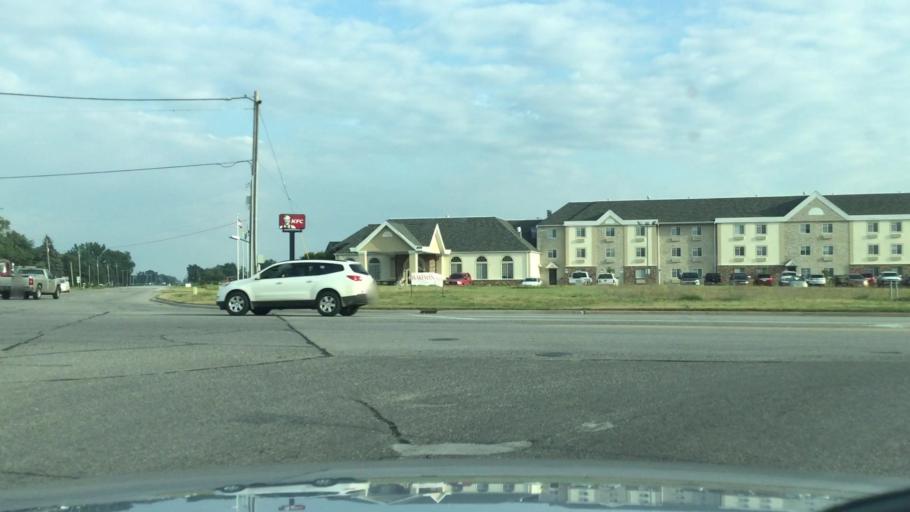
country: US
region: Michigan
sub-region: Saginaw County
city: Birch Run
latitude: 43.2504
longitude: -83.7698
